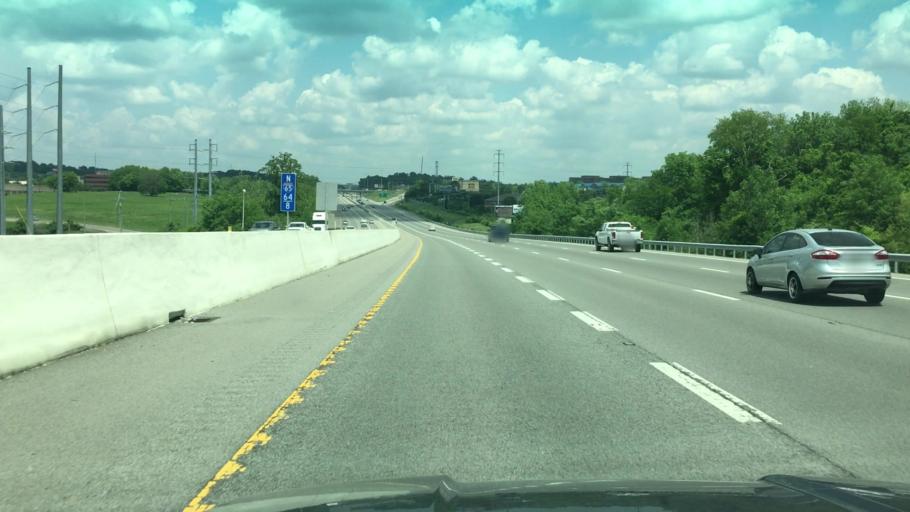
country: US
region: Tennessee
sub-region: Williamson County
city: Franklin
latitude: 35.9045
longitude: -86.8258
